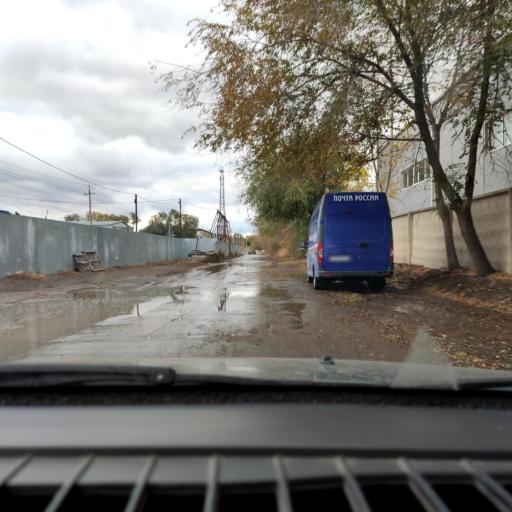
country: RU
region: Samara
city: Tol'yatti
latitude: 53.5725
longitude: 49.2830
